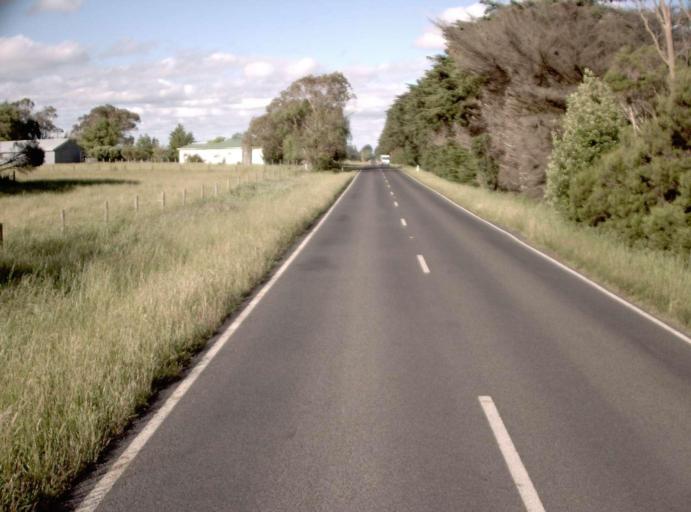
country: AU
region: Victoria
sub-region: Bass Coast
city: North Wonthaggi
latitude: -38.5227
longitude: 145.8905
